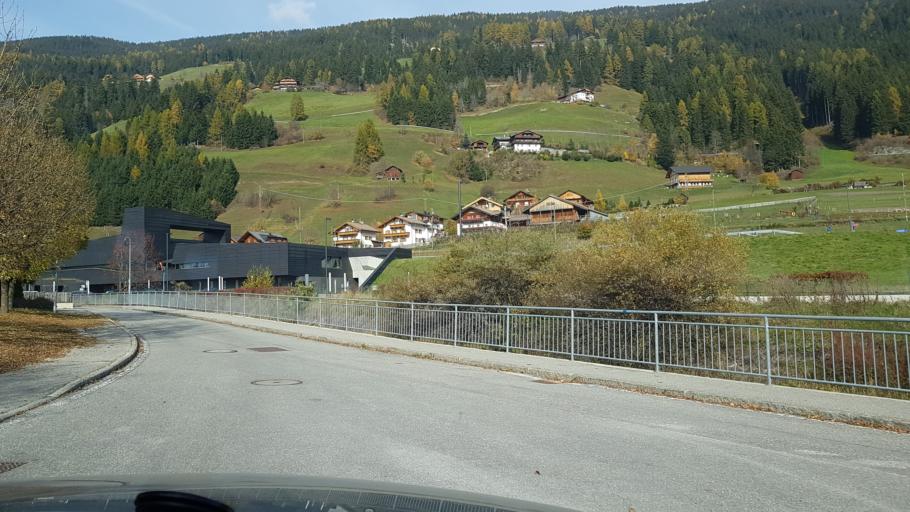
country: IT
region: Trentino-Alto Adige
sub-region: Bolzano
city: San Candido
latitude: 46.7332
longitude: 12.2885
